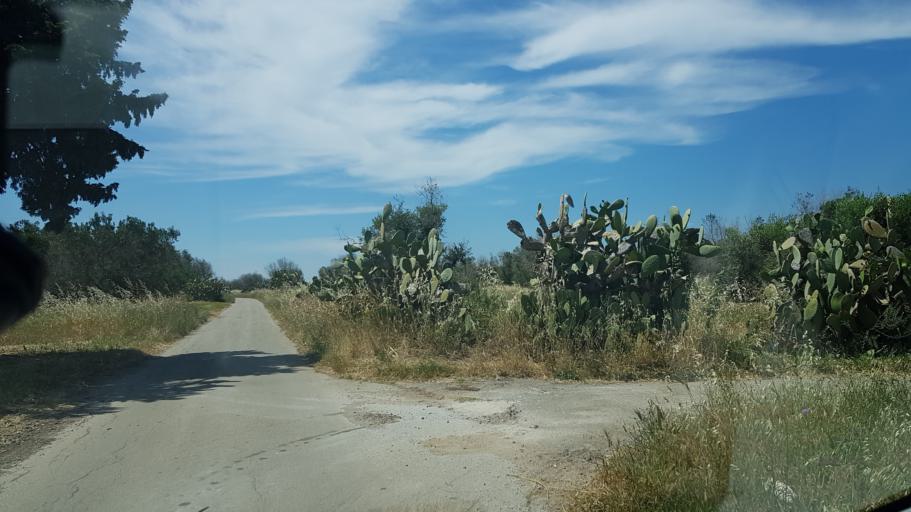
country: IT
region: Apulia
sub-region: Provincia di Brindisi
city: San Pietro Vernotico
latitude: 40.5283
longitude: 18.0045
